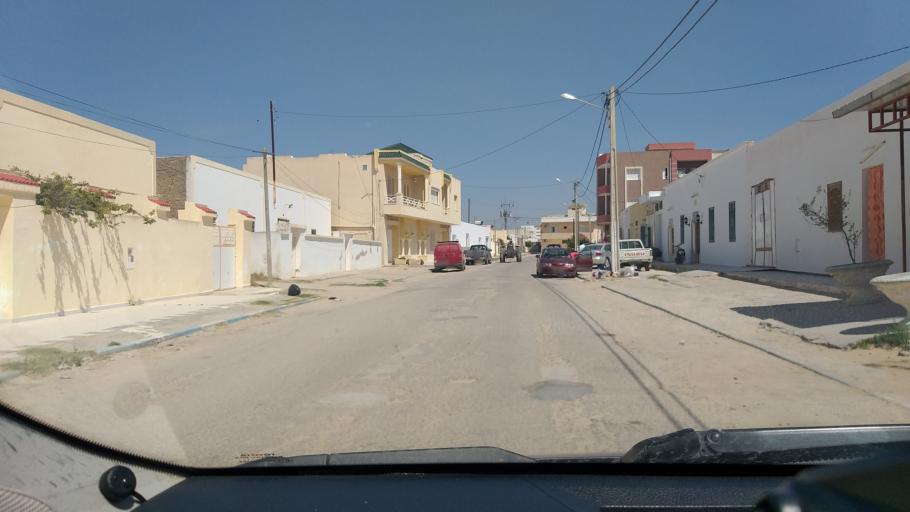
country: TN
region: Al Mahdiyah
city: El Jem
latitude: 35.2926
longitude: 10.7135
